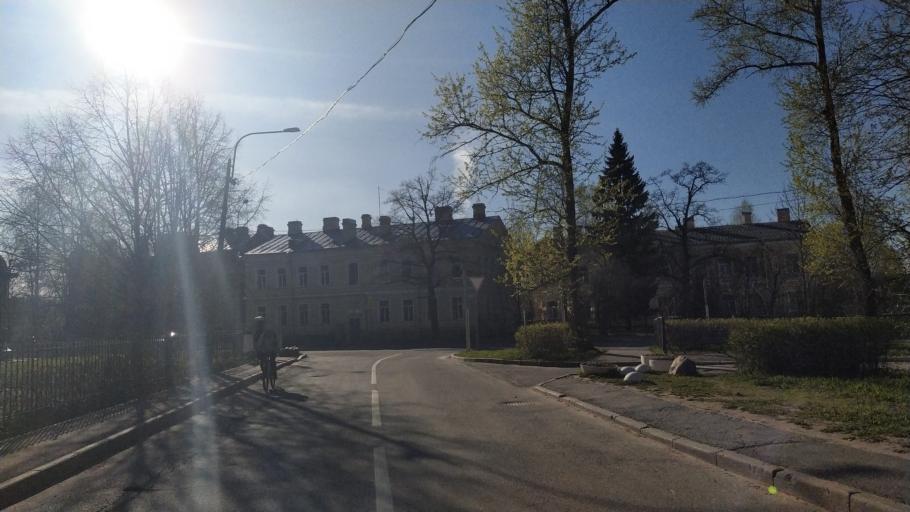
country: RU
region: St.-Petersburg
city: Pushkin
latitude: 59.7078
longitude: 30.3808
